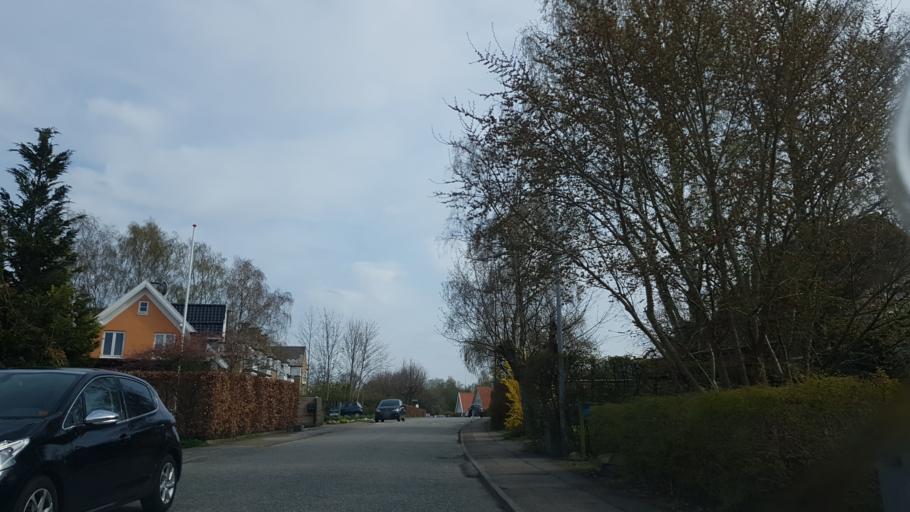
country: DK
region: Capital Region
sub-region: Allerod Kommune
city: Lillerod
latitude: 55.8673
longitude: 12.3588
